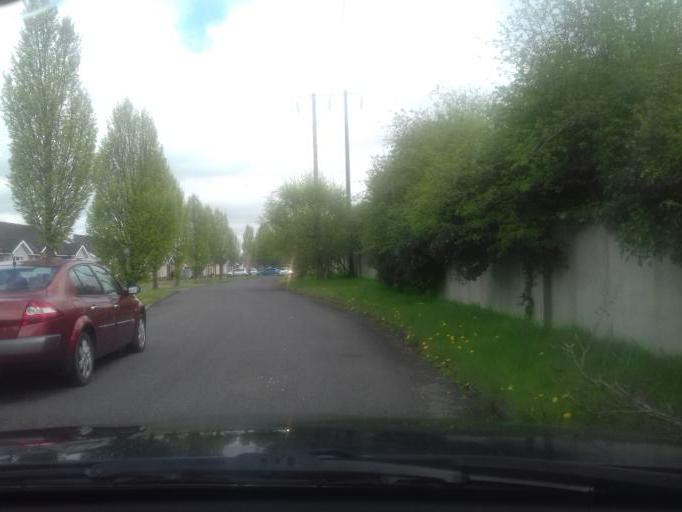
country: IE
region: Leinster
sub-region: Laois
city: Portlaoise
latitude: 53.0418
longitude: -7.3144
